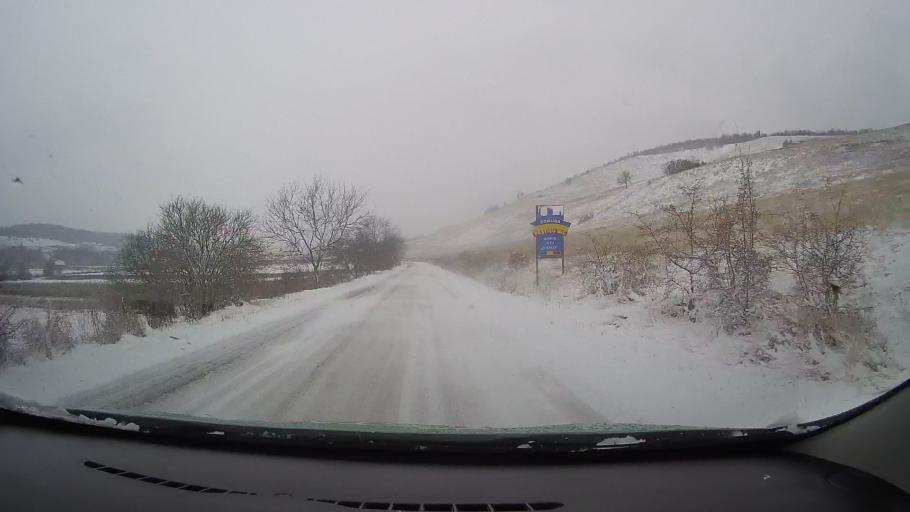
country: RO
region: Hunedoara
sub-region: Comuna Pestisu Mic
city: Pestisu Mic
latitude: 45.7964
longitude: 22.9041
